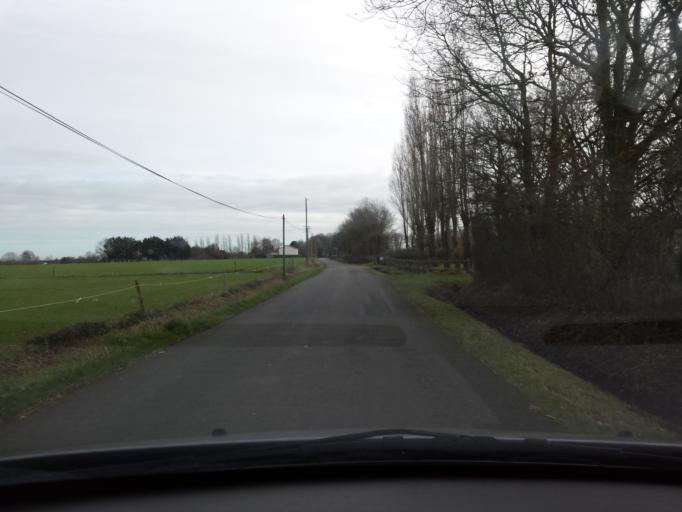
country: FR
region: Pays de la Loire
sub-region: Departement de la Vendee
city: Les Essarts
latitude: 46.7582
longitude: -1.2578
